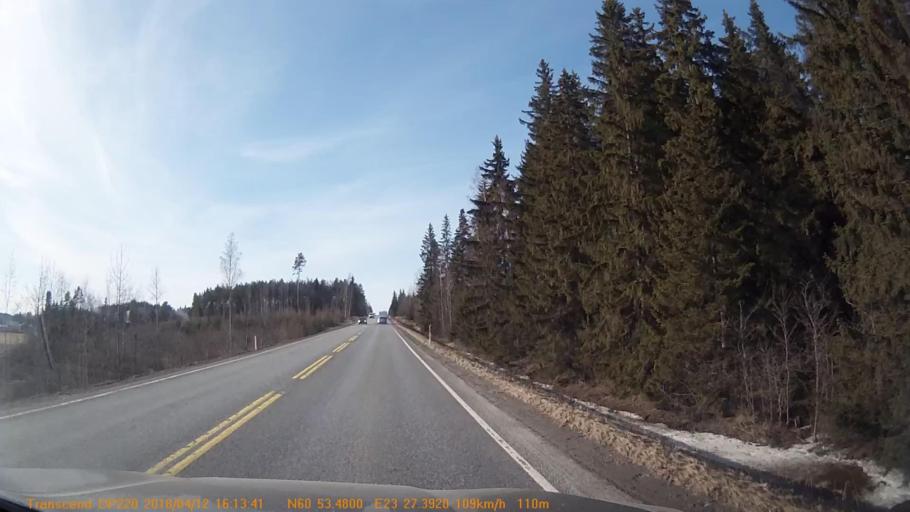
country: FI
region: Haeme
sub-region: Forssa
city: Jokioinen
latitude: 60.8916
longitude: 23.4561
